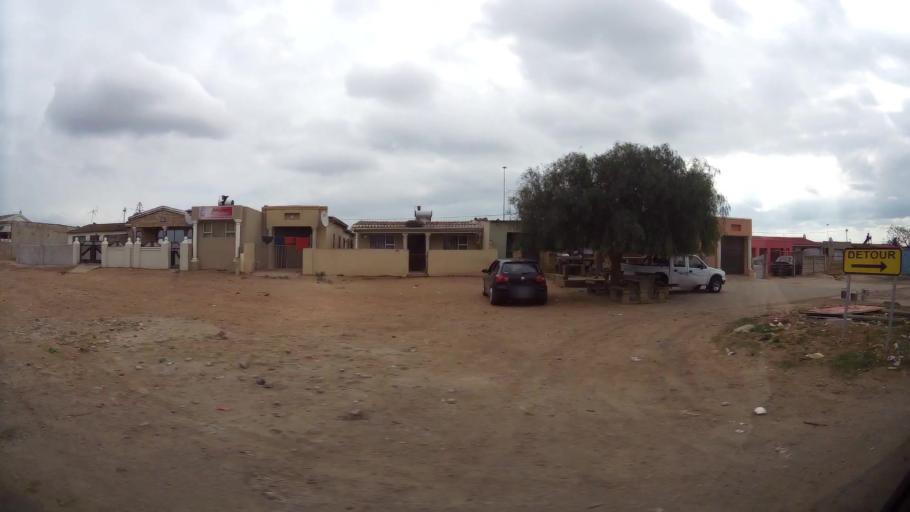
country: ZA
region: Eastern Cape
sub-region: Nelson Mandela Bay Metropolitan Municipality
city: Port Elizabeth
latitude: -33.8725
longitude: 25.5644
